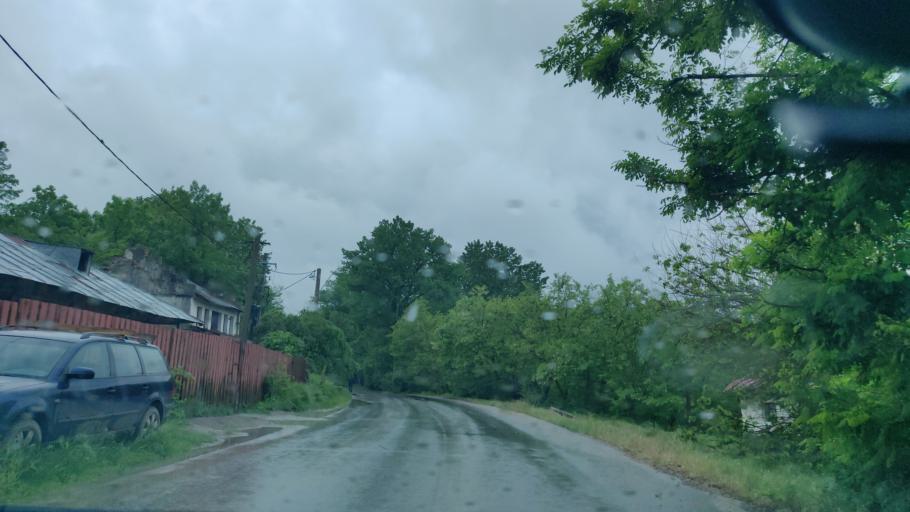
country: RO
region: Giurgiu
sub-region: Comuna Bulbucata
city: Bulbucata
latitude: 44.2885
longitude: 25.7926
